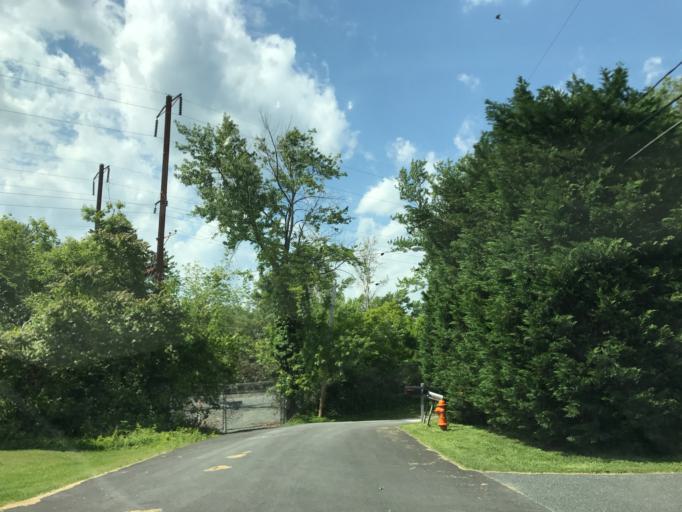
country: US
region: Maryland
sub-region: Baltimore County
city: Bowleys Quarters
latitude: 39.3789
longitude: -76.3542
